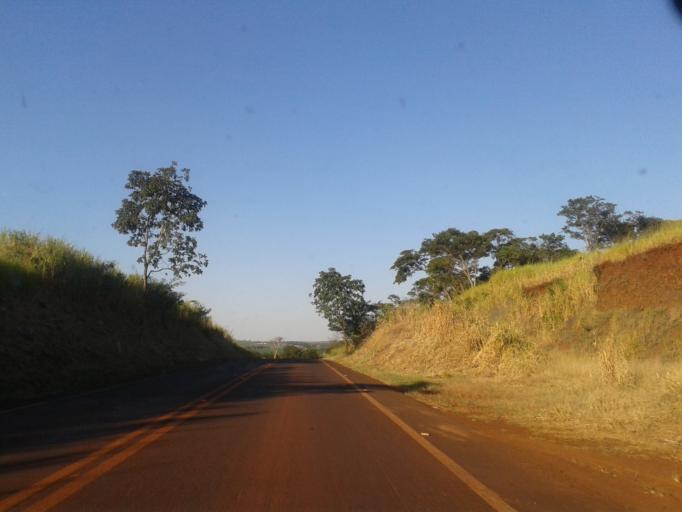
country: BR
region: Minas Gerais
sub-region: Capinopolis
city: Capinopolis
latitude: -18.6934
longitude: -49.6231
